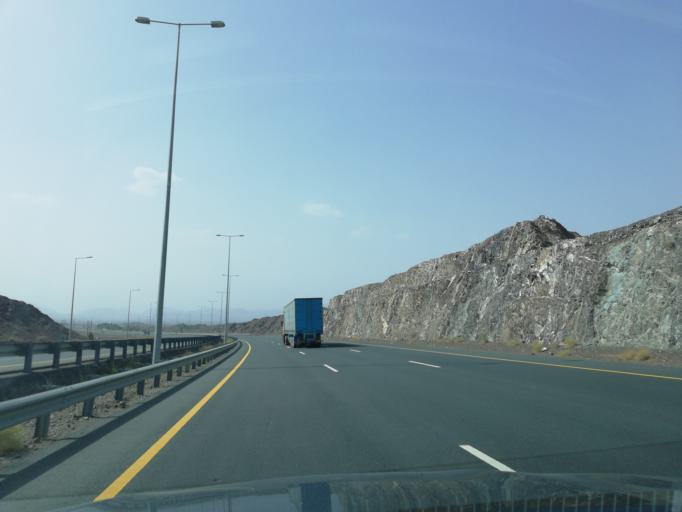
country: OM
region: Muhafazat ad Dakhiliyah
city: Sufalat Sama'il
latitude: 23.0009
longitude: 58.2308
